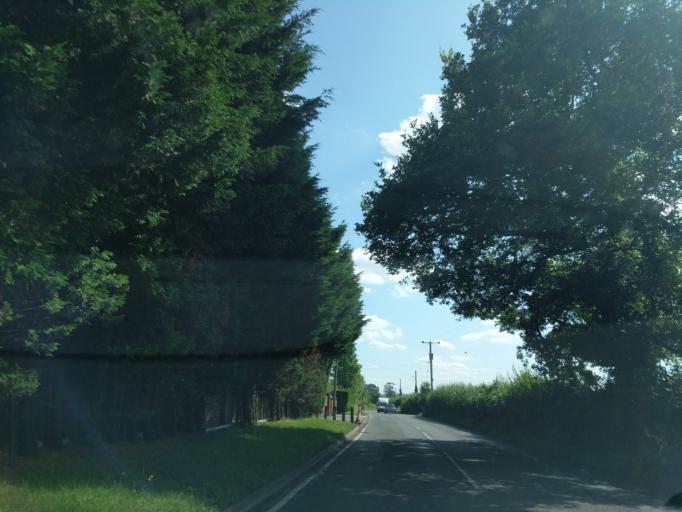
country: GB
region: England
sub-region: Staffordshire
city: Rugeley
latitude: 52.7879
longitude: -1.9371
